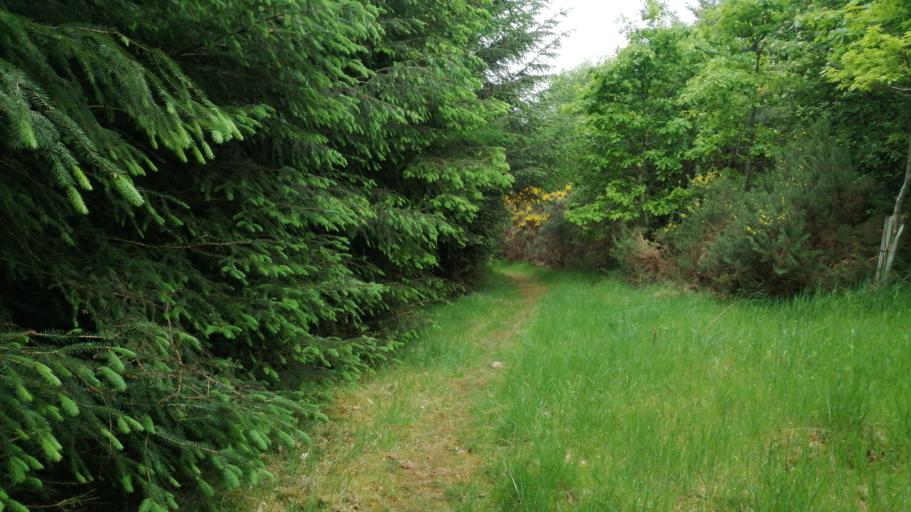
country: GB
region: Scotland
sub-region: Moray
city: Cullen
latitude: 57.5789
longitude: -2.7834
